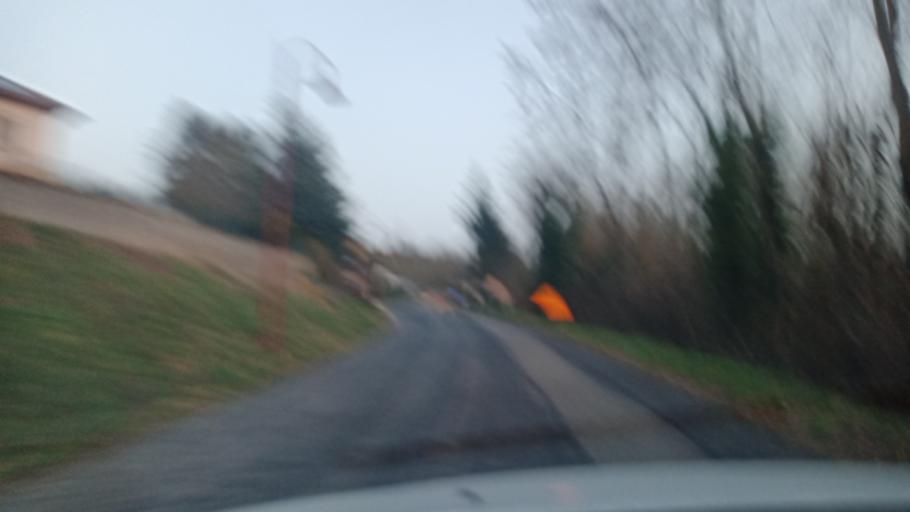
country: FR
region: Rhone-Alpes
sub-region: Departement de l'Isere
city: Roybon
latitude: 45.2560
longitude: 5.2458
